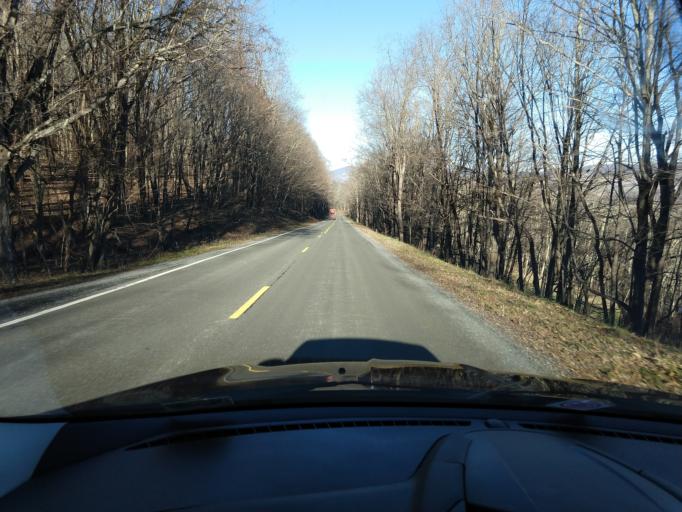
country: US
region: Virginia
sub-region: Highland County
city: Monterey
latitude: 38.4382
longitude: -79.6419
